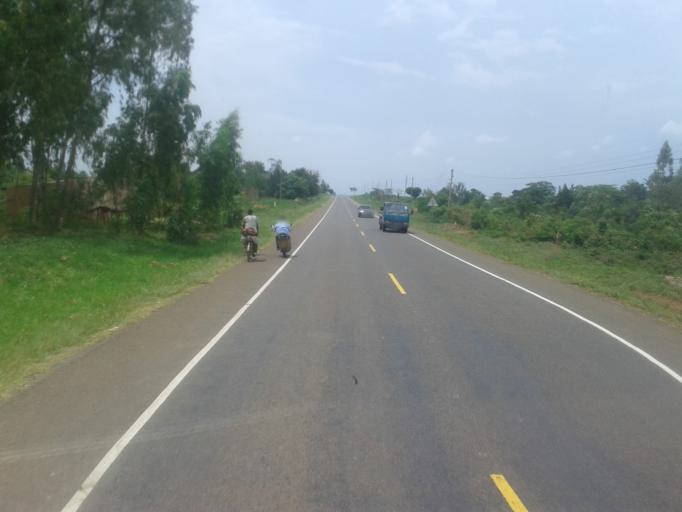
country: UG
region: Western Region
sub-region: Kiryandongo District
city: Kiryandongo
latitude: 1.9031
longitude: 32.0852
